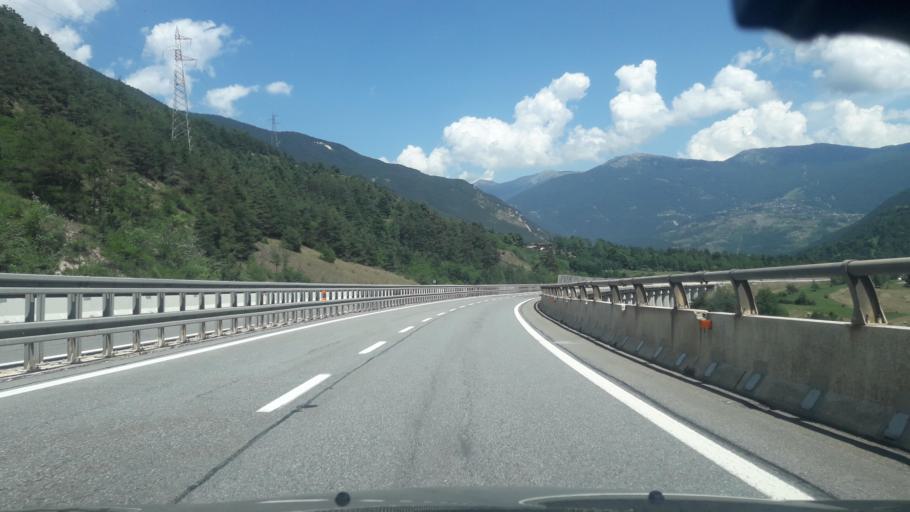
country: IT
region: Piedmont
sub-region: Provincia di Torino
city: Oulx
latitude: 45.0469
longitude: 6.7715
